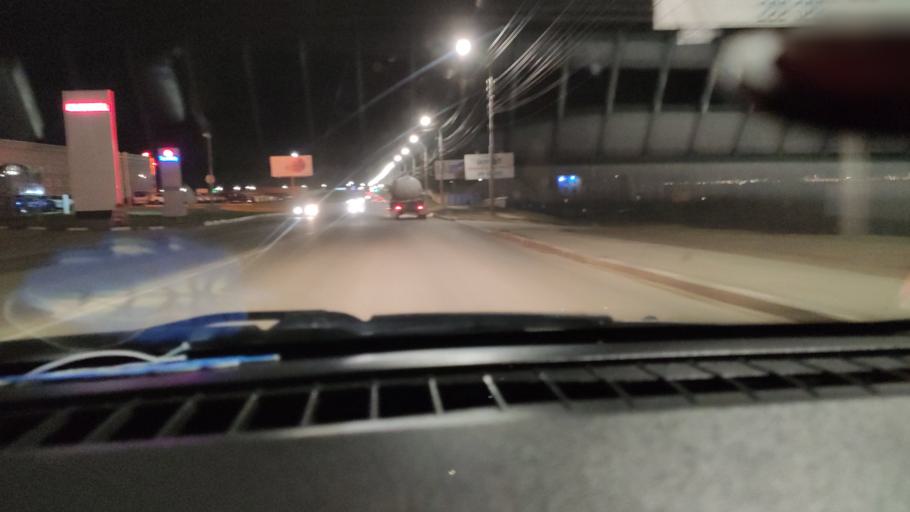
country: RU
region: Saratov
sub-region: Saratovskiy Rayon
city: Saratov
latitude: 51.5576
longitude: 46.0562
